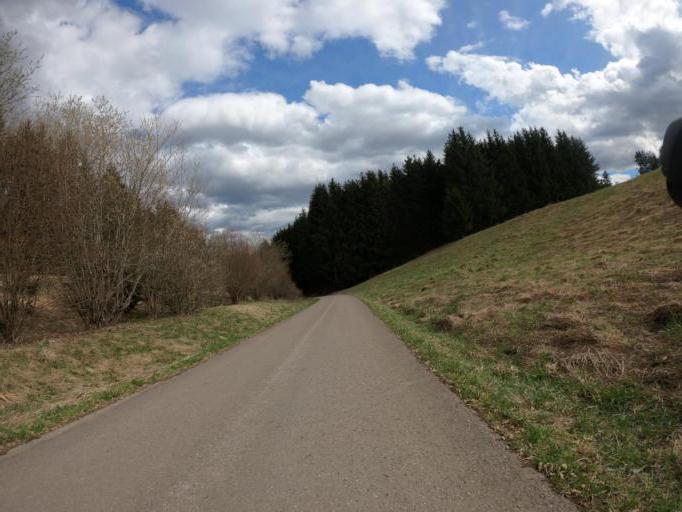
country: DE
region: Baden-Wuerttemberg
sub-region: Tuebingen Region
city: Trochtelfingen
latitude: 48.3770
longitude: 9.2104
